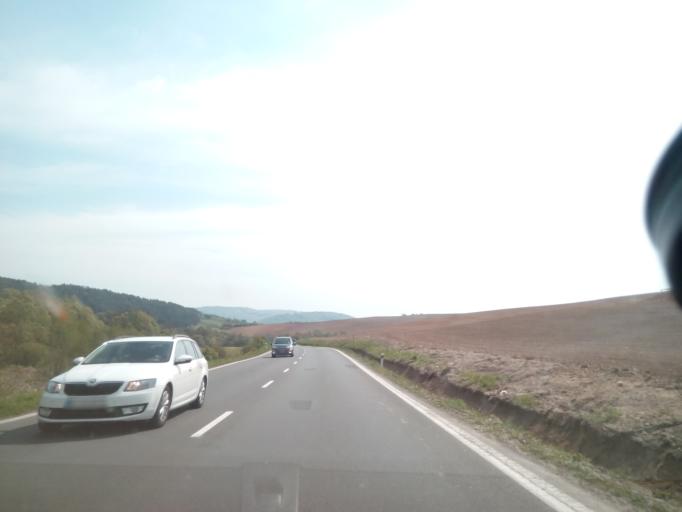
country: SK
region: Presovsky
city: Giraltovce
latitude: 49.0300
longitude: 21.4802
